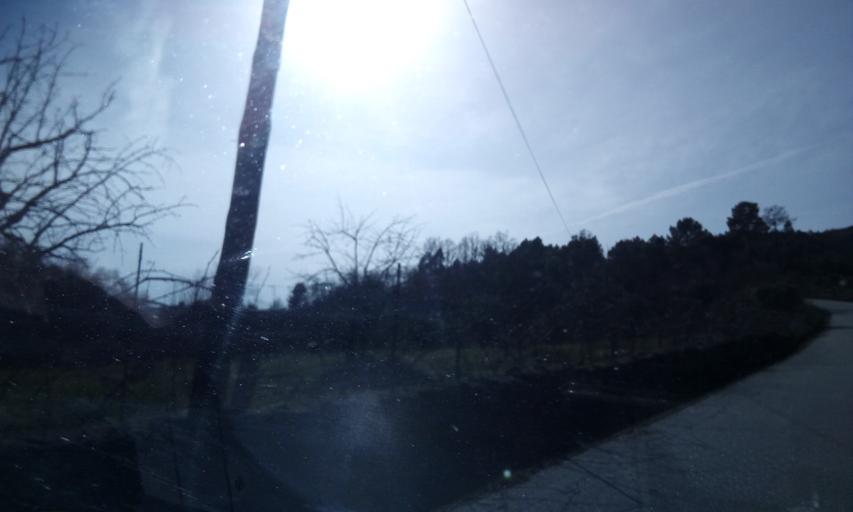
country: PT
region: Guarda
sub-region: Celorico da Beira
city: Celorico da Beira
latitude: 40.6498
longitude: -7.4240
